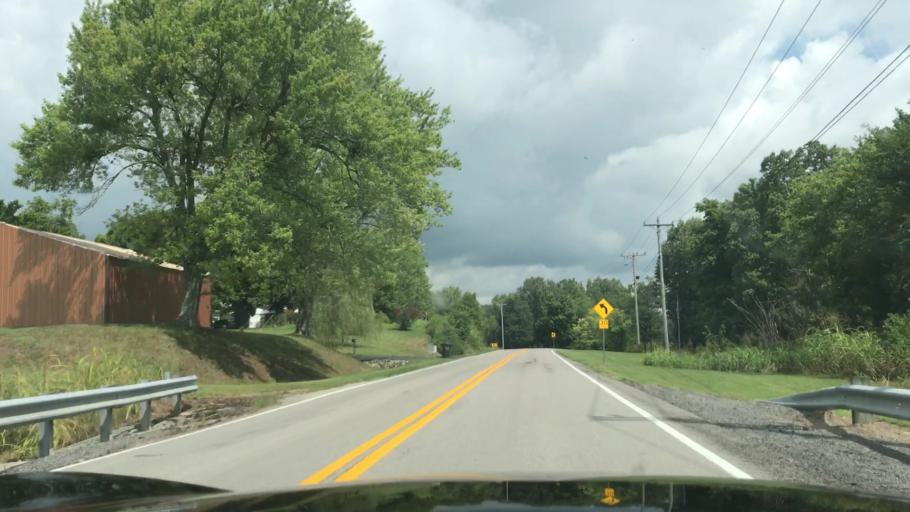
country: US
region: Kentucky
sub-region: Ohio County
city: Beaver Dam
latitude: 37.2122
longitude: -86.9013
